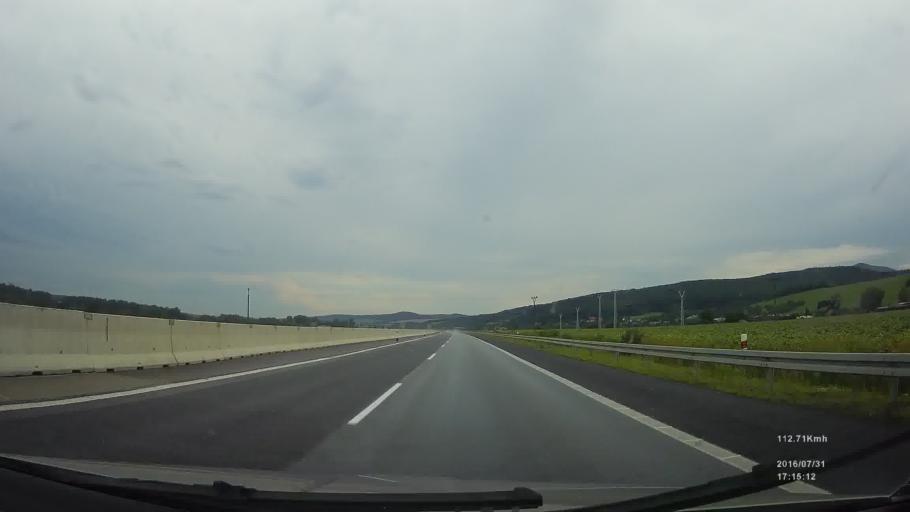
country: SK
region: Presovsky
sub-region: Okres Presov
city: Presov
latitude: 48.9122
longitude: 21.2508
